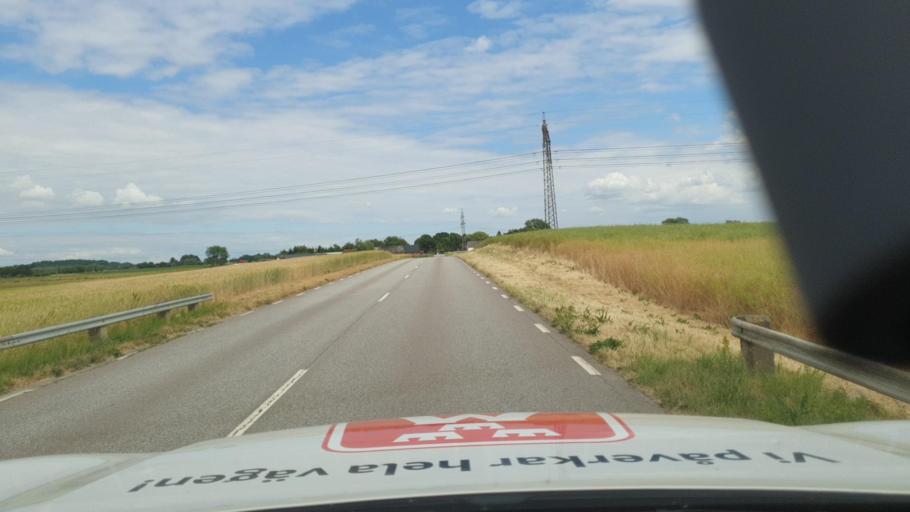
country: SE
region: Skane
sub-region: Svedala Kommun
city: Svedala
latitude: 55.5229
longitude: 13.1768
